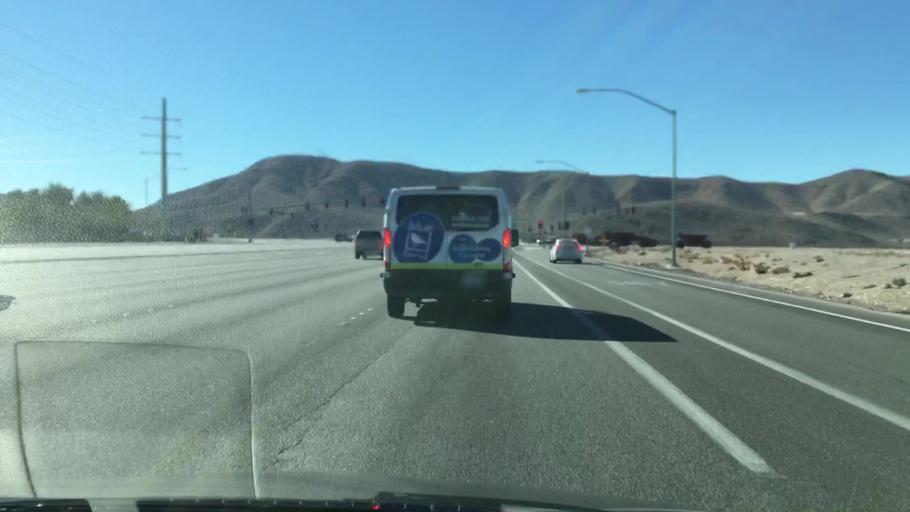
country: US
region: Nevada
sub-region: Clark County
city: Enterprise
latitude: 35.9669
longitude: -115.1712
